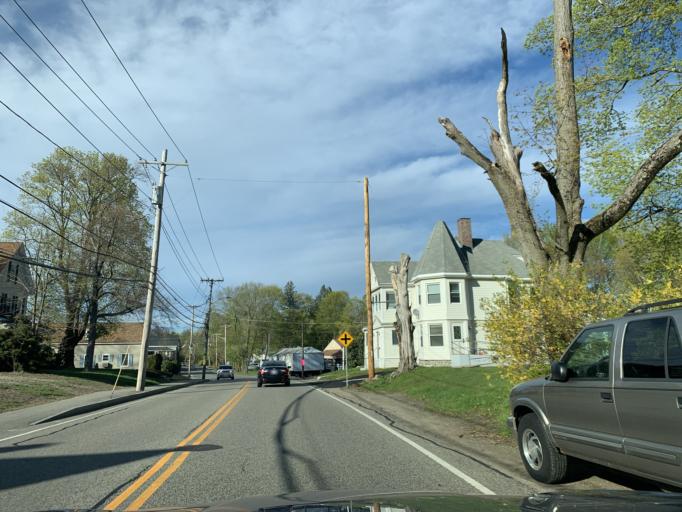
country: US
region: Massachusetts
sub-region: Norfolk County
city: Stoughton
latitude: 42.1283
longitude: -71.0951
